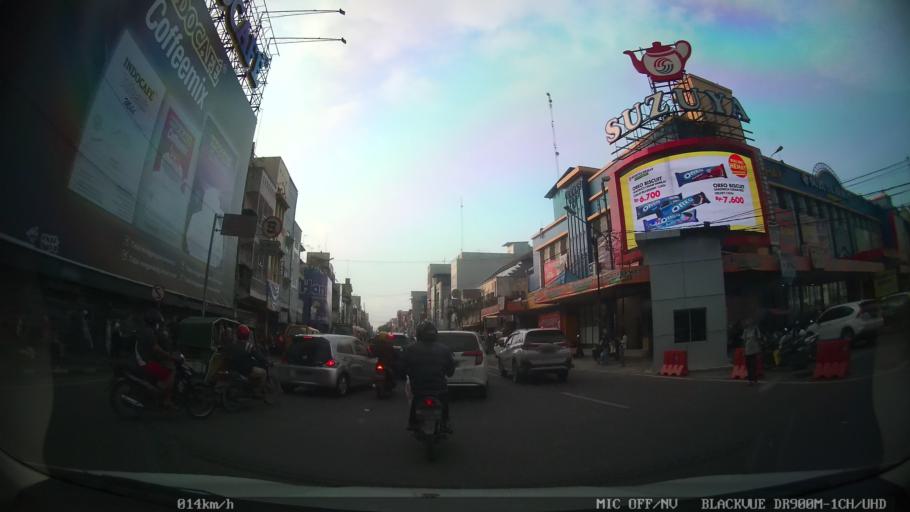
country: ID
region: North Sumatra
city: Medan
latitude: 3.5870
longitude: 98.6858
